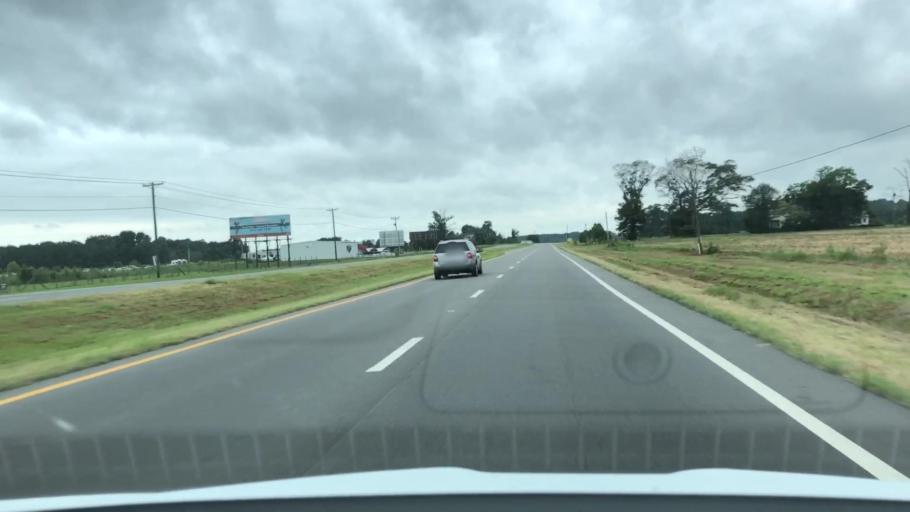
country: US
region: North Carolina
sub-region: Lenoir County
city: La Grange
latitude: 35.2605
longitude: -77.6968
